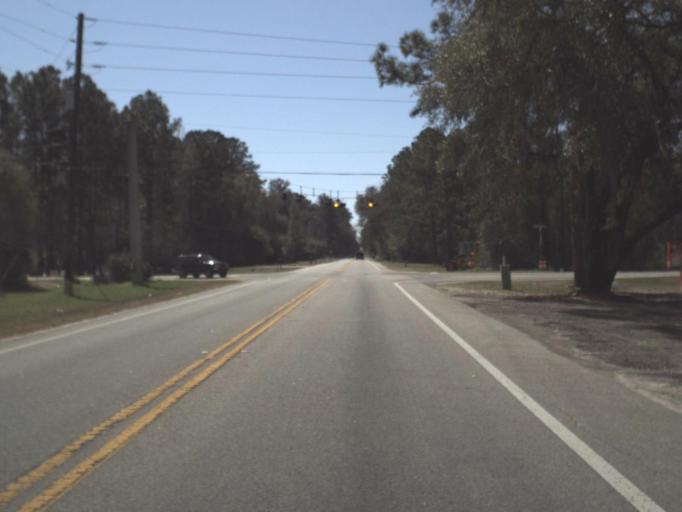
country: US
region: Florida
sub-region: Leon County
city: Woodville
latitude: 30.3254
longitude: -84.3115
